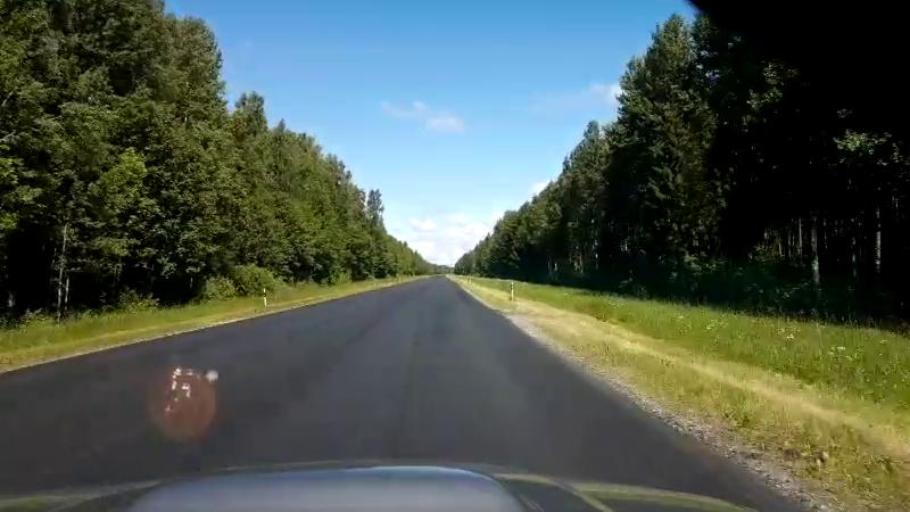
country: LV
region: Salacgrivas
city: Ainazi
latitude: 57.9573
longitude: 24.4413
